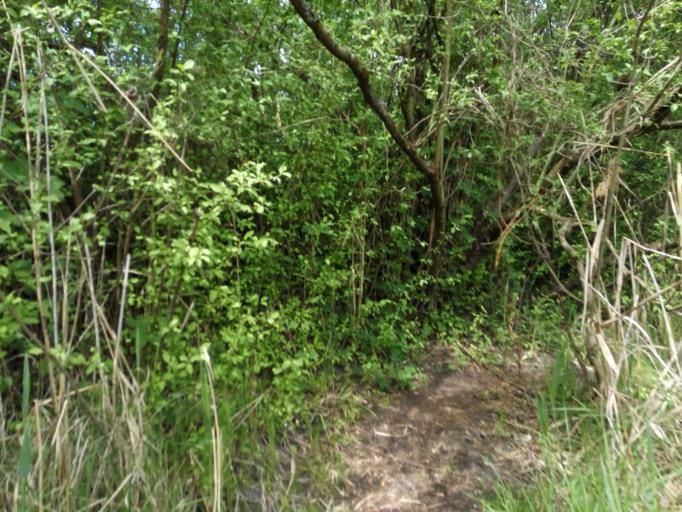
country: DE
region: Berlin
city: Mahlsdorf
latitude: 52.4961
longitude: 13.5968
